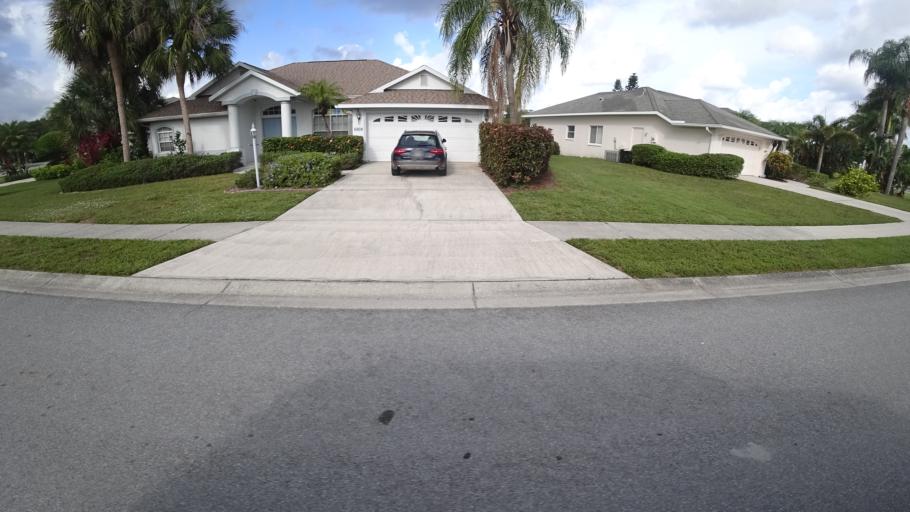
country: US
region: Florida
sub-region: Sarasota County
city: Desoto Lakes
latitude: 27.4171
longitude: -82.4869
